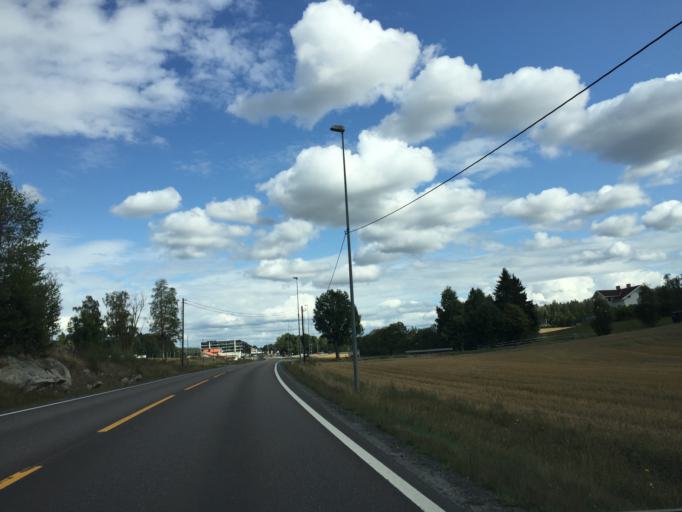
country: NO
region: Ostfold
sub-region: Hobol
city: Knappstad
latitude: 59.6200
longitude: 11.0159
